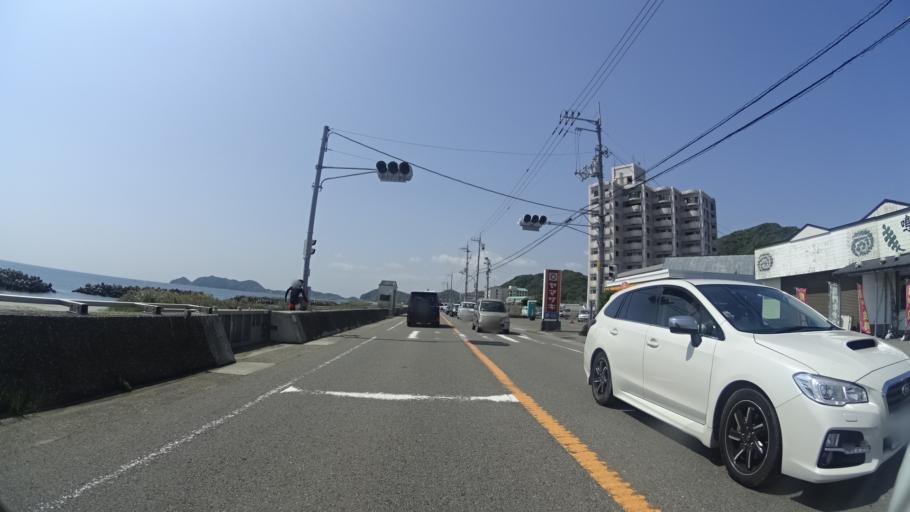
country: JP
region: Tokushima
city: Narutocho-mitsuishi
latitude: 34.2102
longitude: 134.6279
